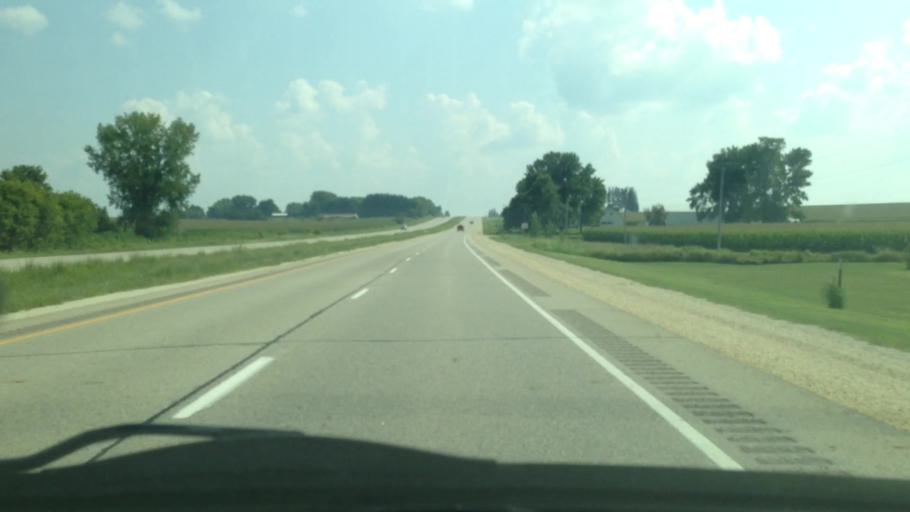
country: US
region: Iowa
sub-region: Bremer County
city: Denver
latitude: 42.6417
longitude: -92.3377
